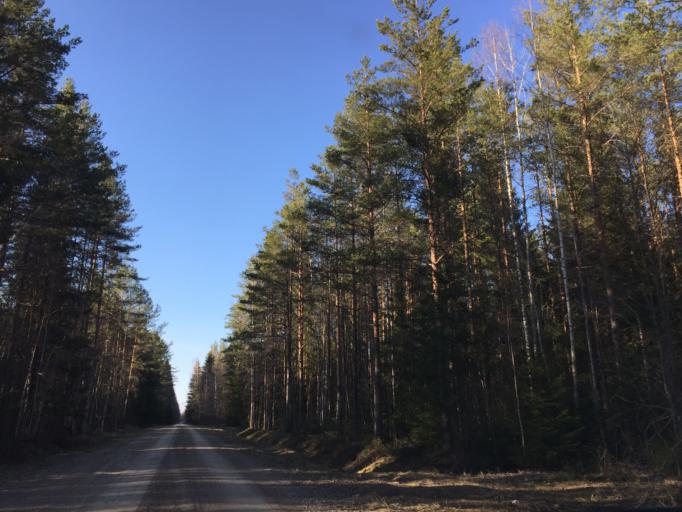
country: EE
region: Ida-Virumaa
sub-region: Sillamaee linn
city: Sillamae
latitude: 59.1599
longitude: 27.8006
